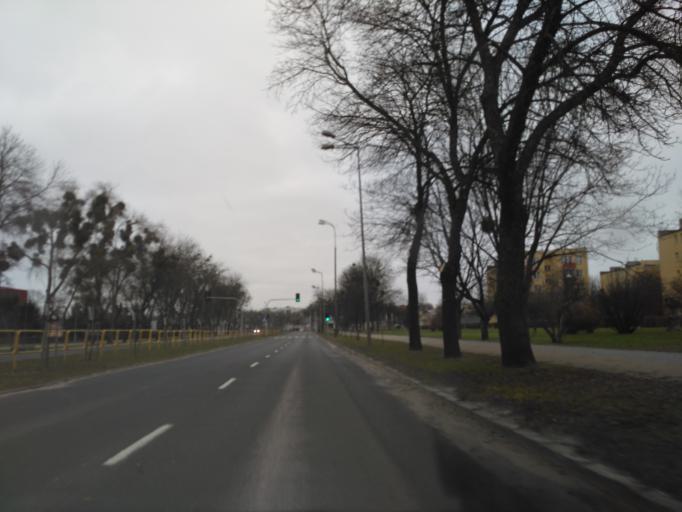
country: PL
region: Lublin Voivodeship
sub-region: Chelm
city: Chelm
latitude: 51.1280
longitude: 23.4778
